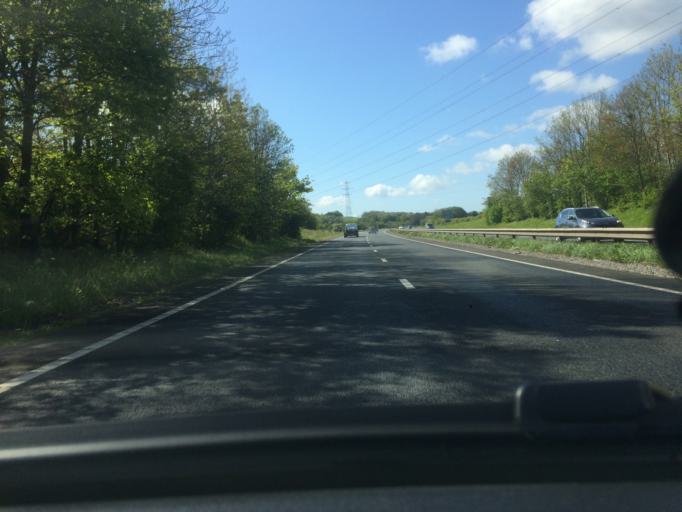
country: GB
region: Wales
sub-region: Wrexham
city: Ruabon
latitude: 53.0046
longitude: -3.0232
